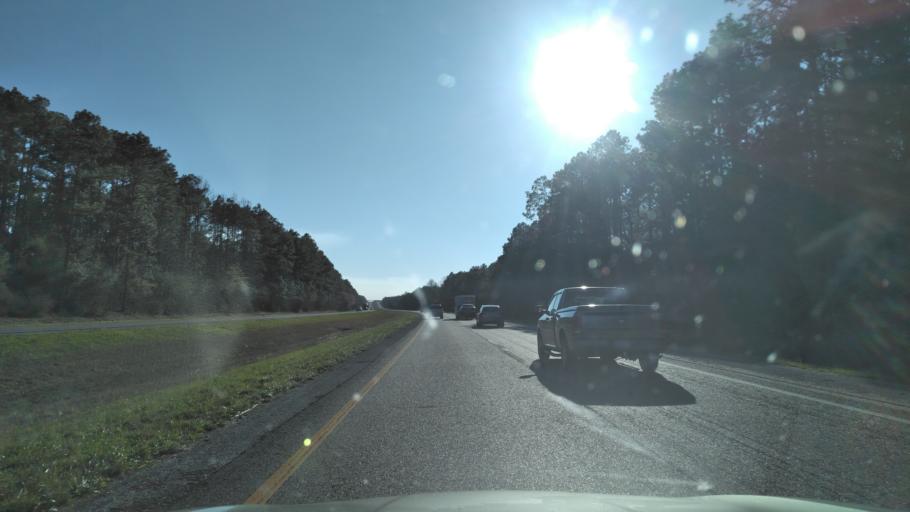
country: US
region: Alabama
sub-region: Escambia County
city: Atmore
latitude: 31.0349
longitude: -87.6331
